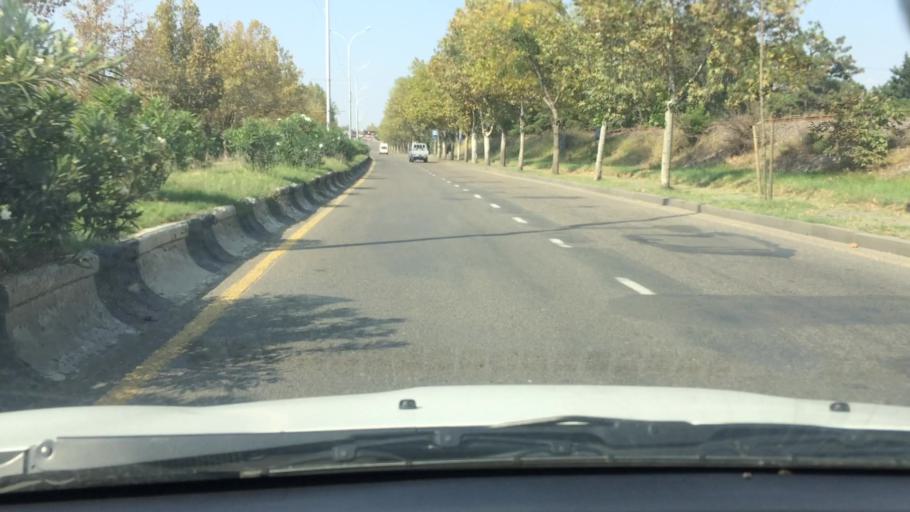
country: GE
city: Didi Lilo
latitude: 41.6790
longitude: 44.9587
